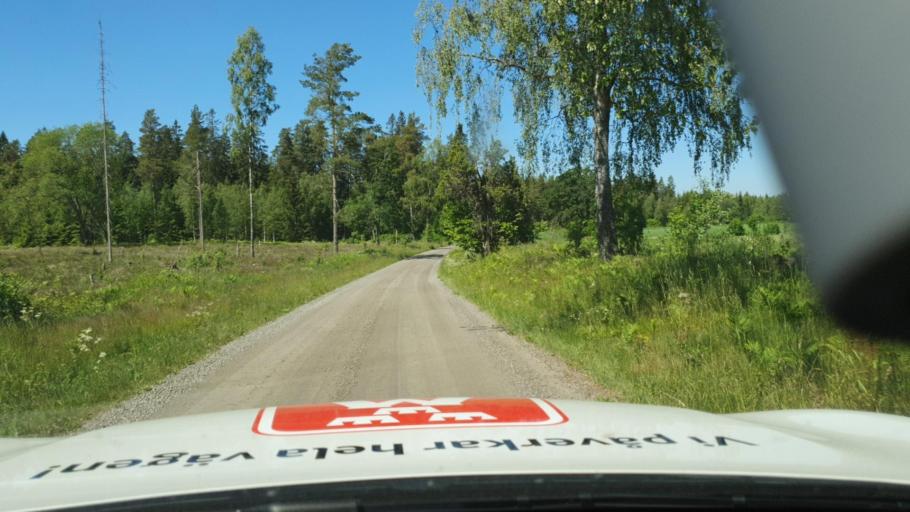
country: SE
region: Joenkoeping
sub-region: Mullsjo Kommun
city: Mullsjoe
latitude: 57.8912
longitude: 13.9435
